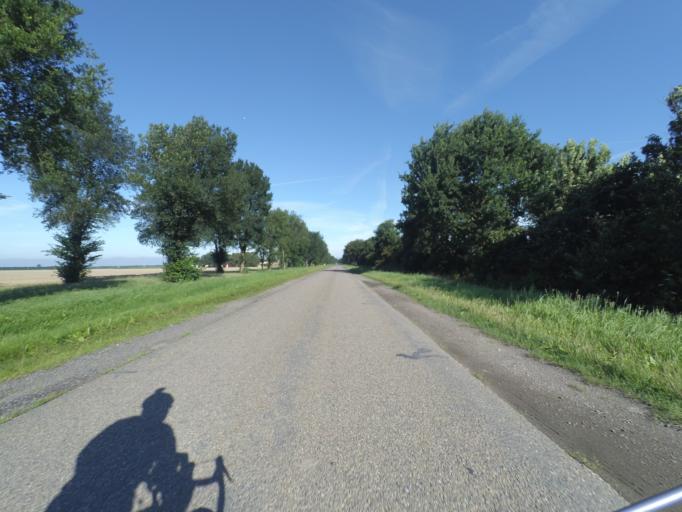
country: NL
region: Flevoland
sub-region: Gemeente Zeewolde
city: Zeewolde
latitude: 52.3835
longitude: 5.4976
